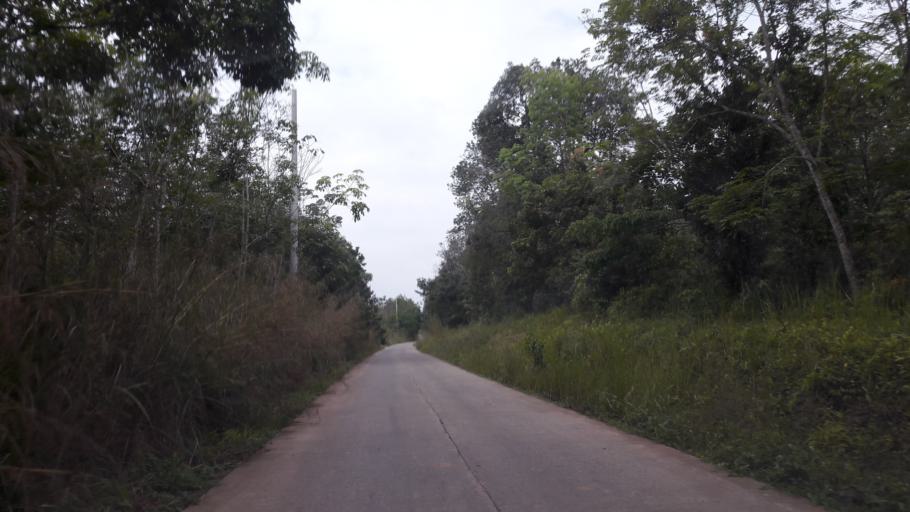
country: ID
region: South Sumatra
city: Gunungmenang
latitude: -3.2434
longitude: 104.1323
